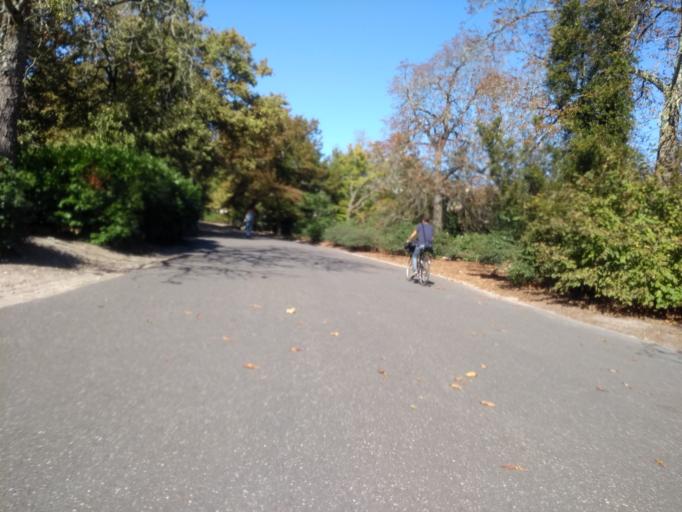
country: FR
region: Aquitaine
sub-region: Departement de la Gironde
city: Le Bouscat
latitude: 44.8543
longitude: -0.5997
